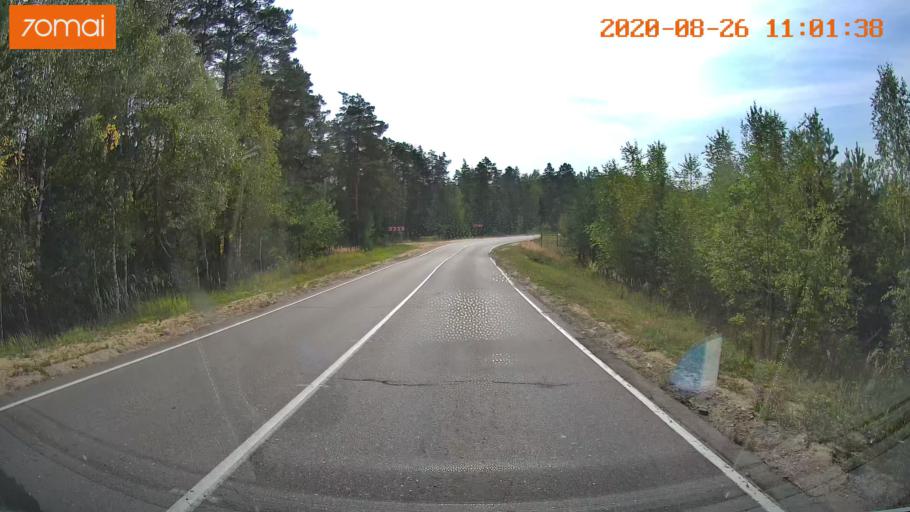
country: RU
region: Rjazan
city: Izhevskoye
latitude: 54.5606
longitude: 41.2267
